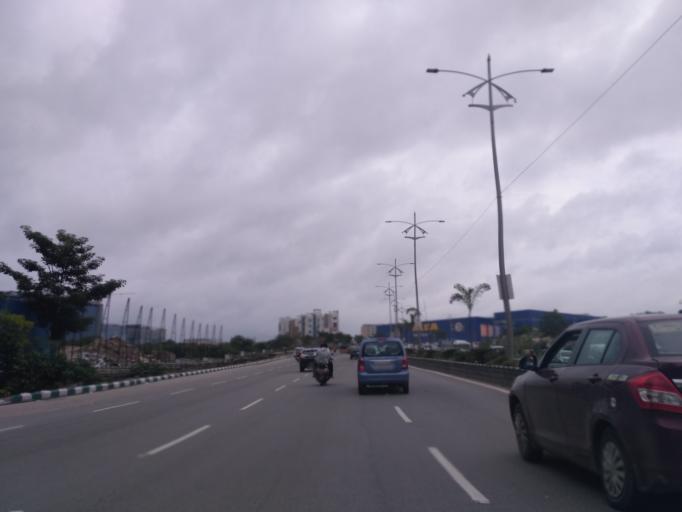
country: IN
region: Telangana
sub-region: Rangareddi
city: Kukatpalli
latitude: 17.4350
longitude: 78.3744
